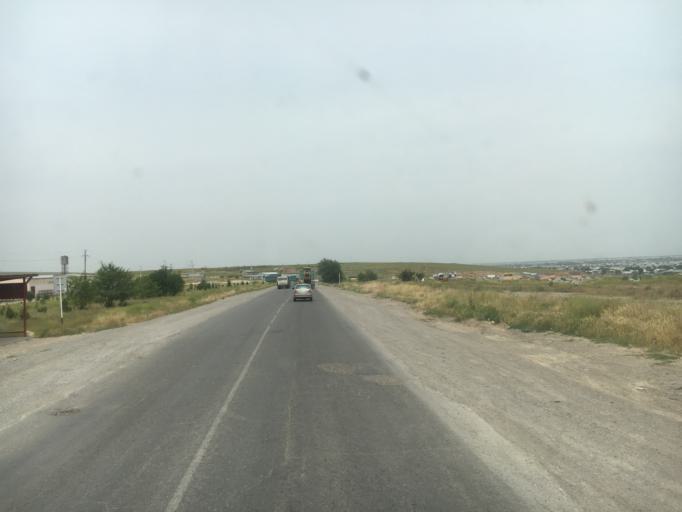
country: KZ
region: Ongtustik Qazaqstan
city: Shymkent
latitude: 42.3215
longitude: 69.5180
